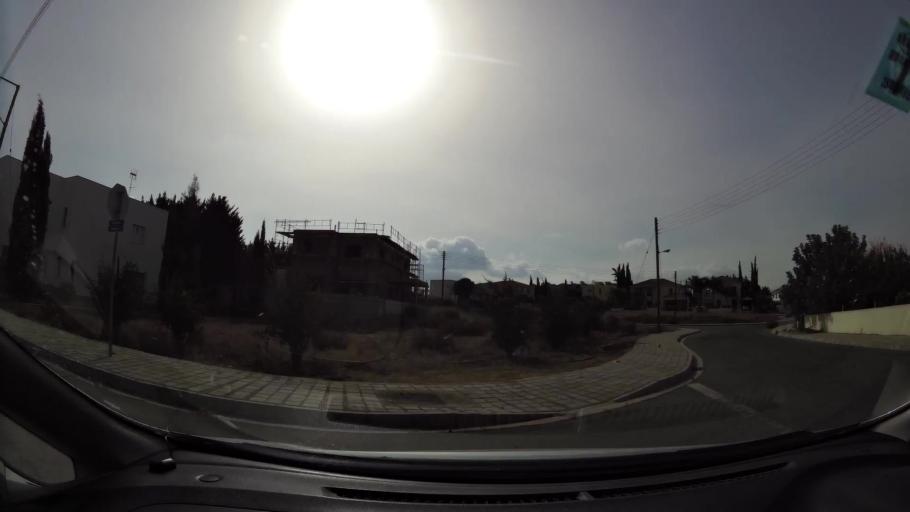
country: CY
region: Lefkosia
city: Geri
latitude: 35.0732
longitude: 33.3949
